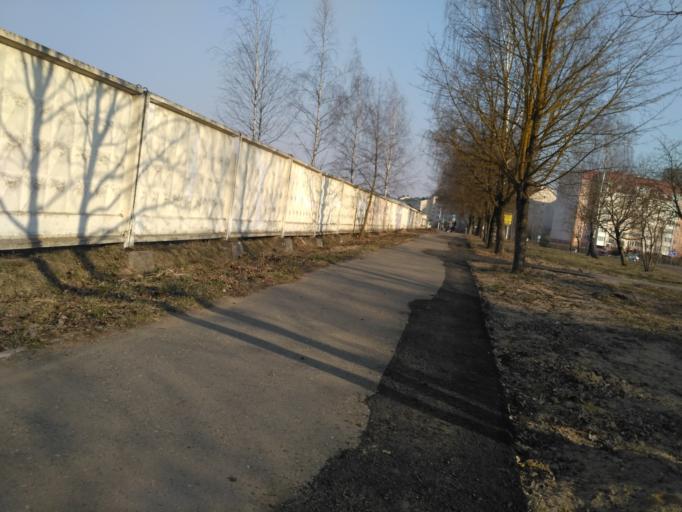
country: BY
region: Minsk
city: Zaslawye
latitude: 54.0155
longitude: 27.2562
